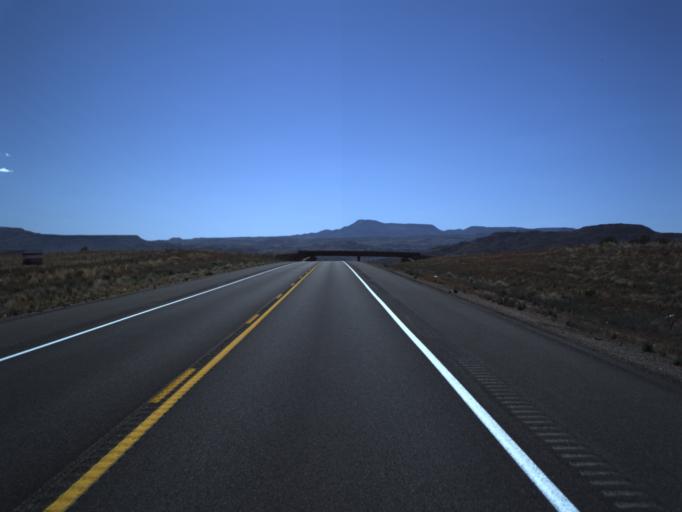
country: US
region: Utah
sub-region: Washington County
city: Washington
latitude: 37.0312
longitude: -113.4852
